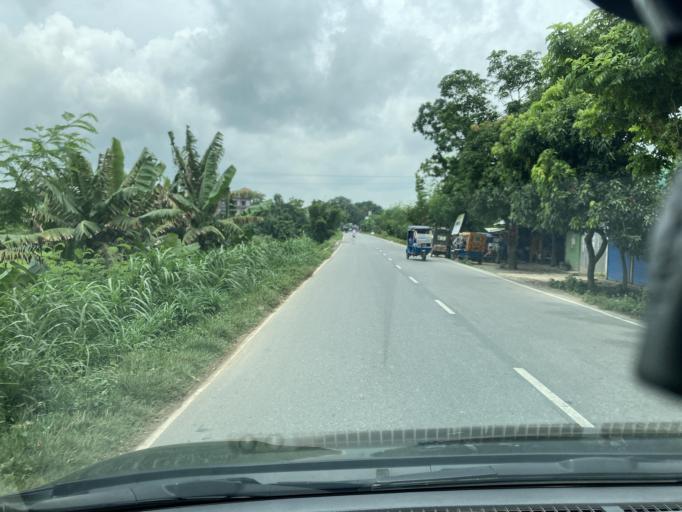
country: BD
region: Dhaka
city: Azimpur
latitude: 23.8062
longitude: 90.2045
